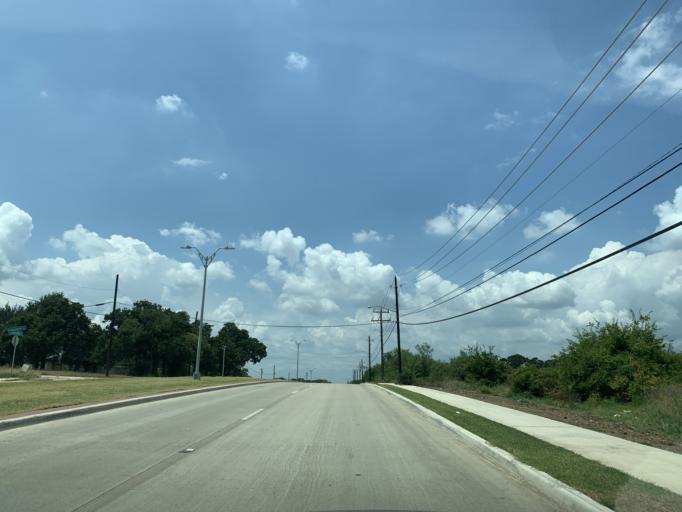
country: US
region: Texas
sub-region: Tarrant County
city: Forest Hill
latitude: 32.7313
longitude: -97.2507
